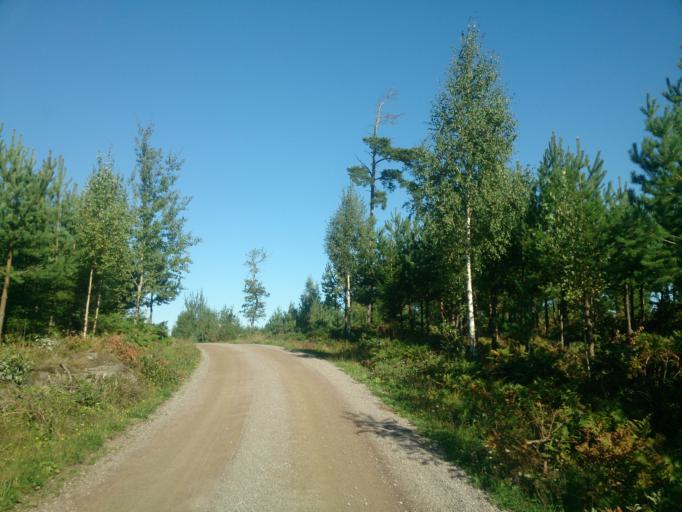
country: SE
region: OEstergoetland
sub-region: Atvidabergs Kommun
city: Atvidaberg
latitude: 58.2645
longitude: 15.9550
